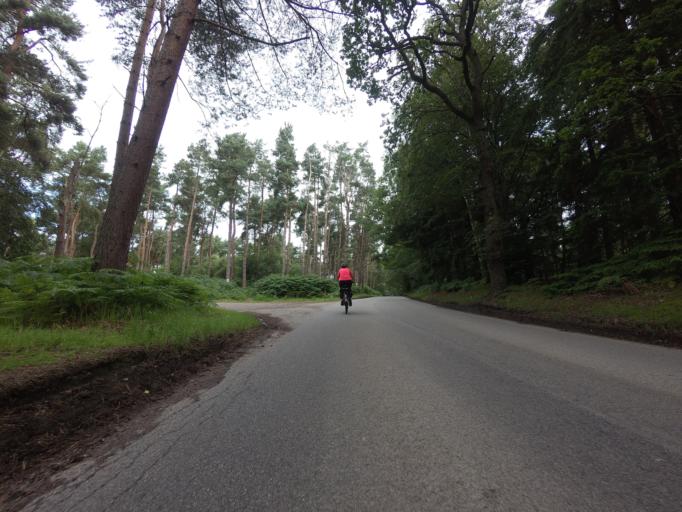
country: GB
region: Scotland
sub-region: Moray
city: Elgin
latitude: 57.6537
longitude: -3.3459
